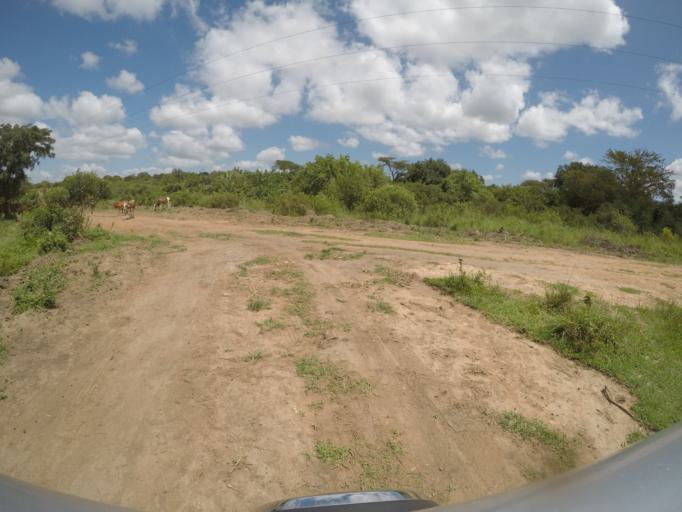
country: ZA
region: KwaZulu-Natal
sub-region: uThungulu District Municipality
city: Empangeni
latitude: -28.5902
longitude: 31.8390
